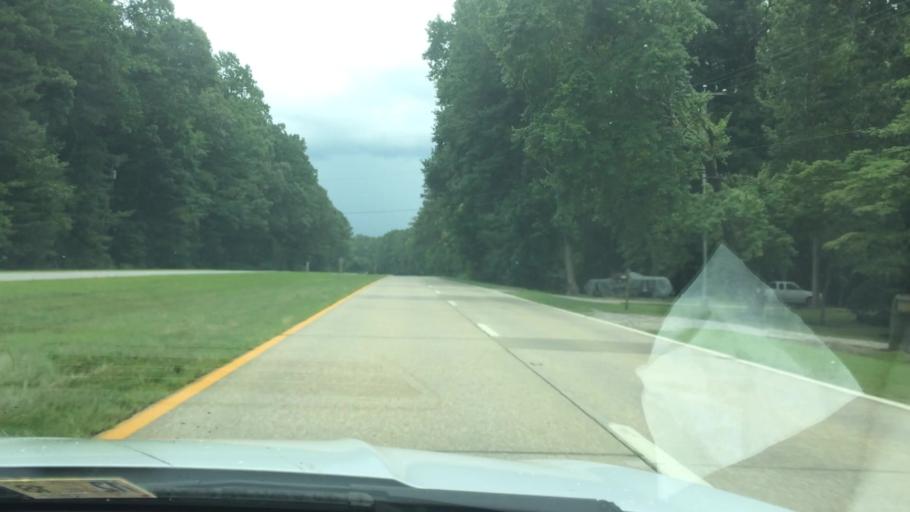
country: US
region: Virginia
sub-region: King William County
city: West Point
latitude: 37.4088
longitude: -76.8566
